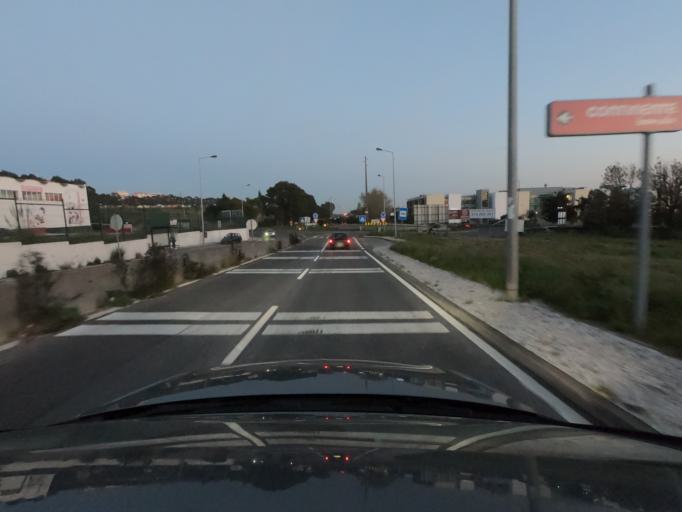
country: PT
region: Lisbon
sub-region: Sintra
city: Cacem
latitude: 38.7517
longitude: -9.3063
